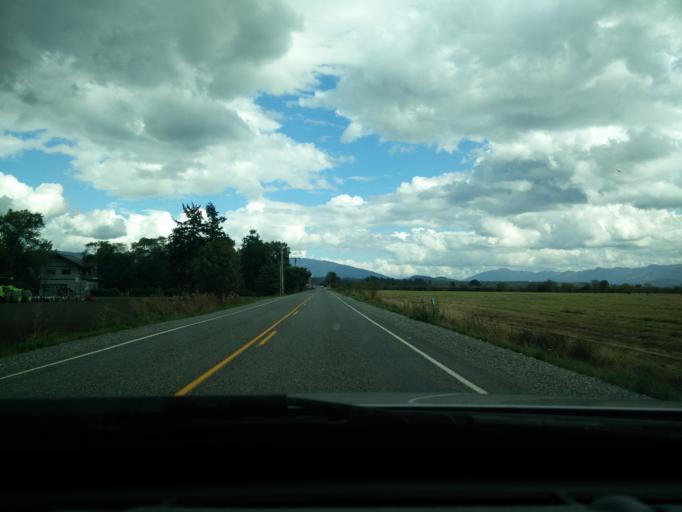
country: US
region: Washington
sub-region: Skagit County
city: Burlington
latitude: 48.5537
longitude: -122.4610
